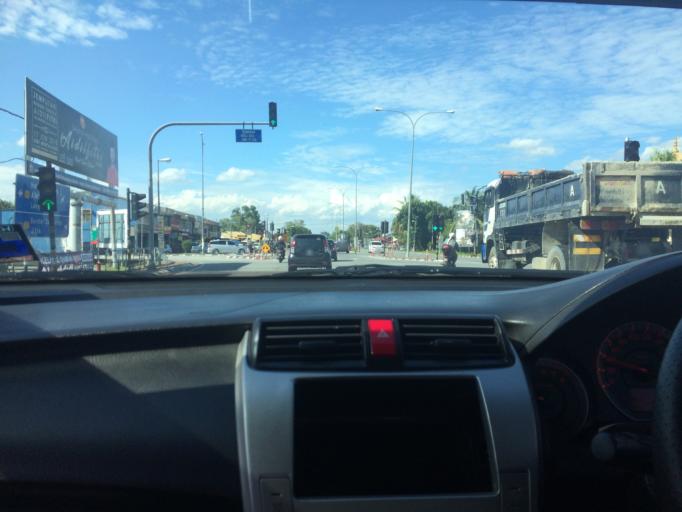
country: MY
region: Kedah
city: Jitra
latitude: 6.2035
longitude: 100.4129
